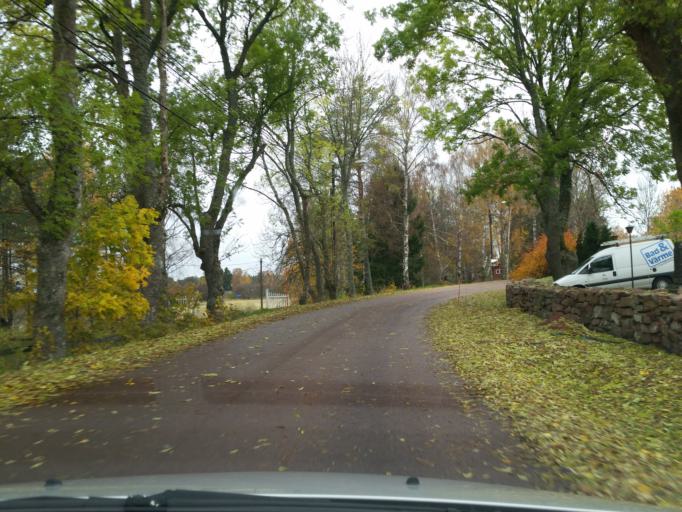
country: AX
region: Alands landsbygd
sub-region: Lemland
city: Lemland
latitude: 60.0745
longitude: 20.0834
